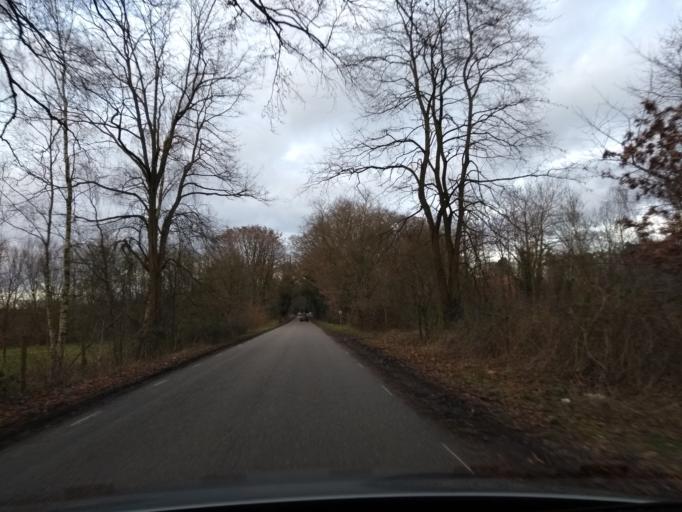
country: NL
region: Overijssel
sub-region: Gemeente Enschede
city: Enschede
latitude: 52.2463
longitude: 6.8845
